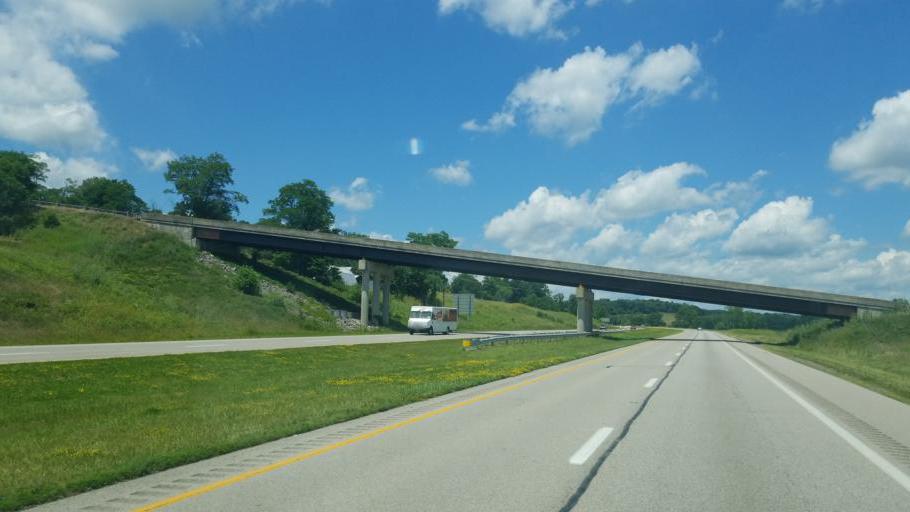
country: US
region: Ohio
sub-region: Gallia County
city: Gallipolis
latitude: 38.8591
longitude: -82.2521
